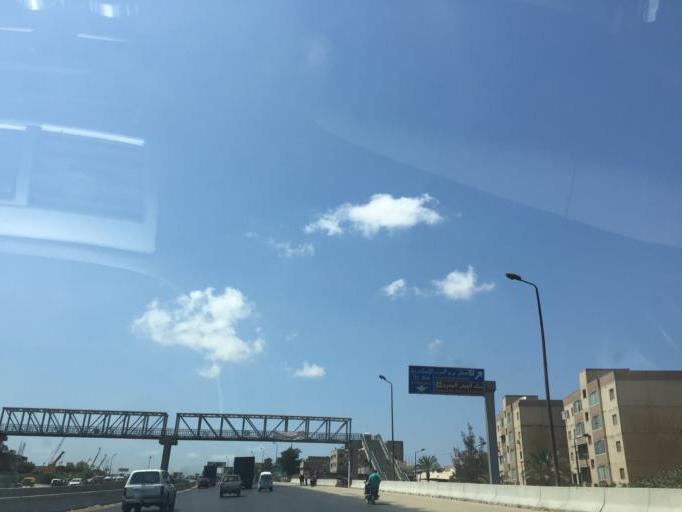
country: EG
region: Alexandria
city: Alexandria
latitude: 31.0253
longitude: 29.7922
